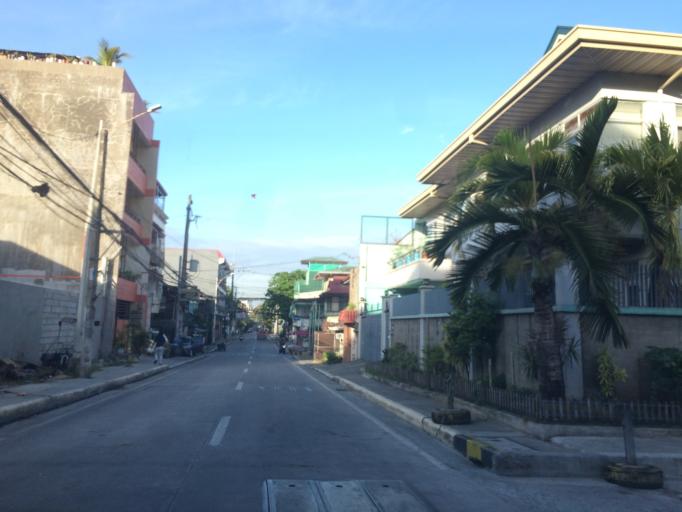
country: PH
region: Metro Manila
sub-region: City of Manila
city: Manila
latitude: 14.6228
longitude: 120.9962
